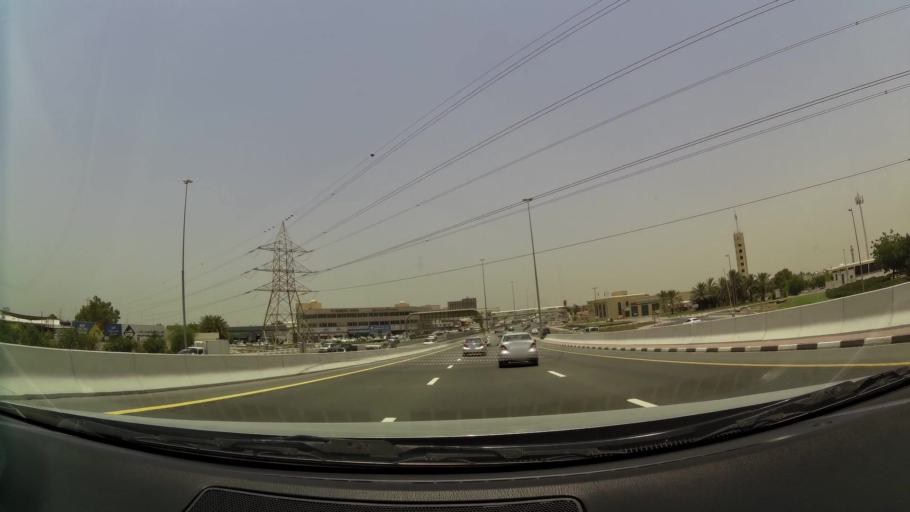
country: AE
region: Ash Shariqah
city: Sharjah
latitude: 25.2212
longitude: 55.3762
